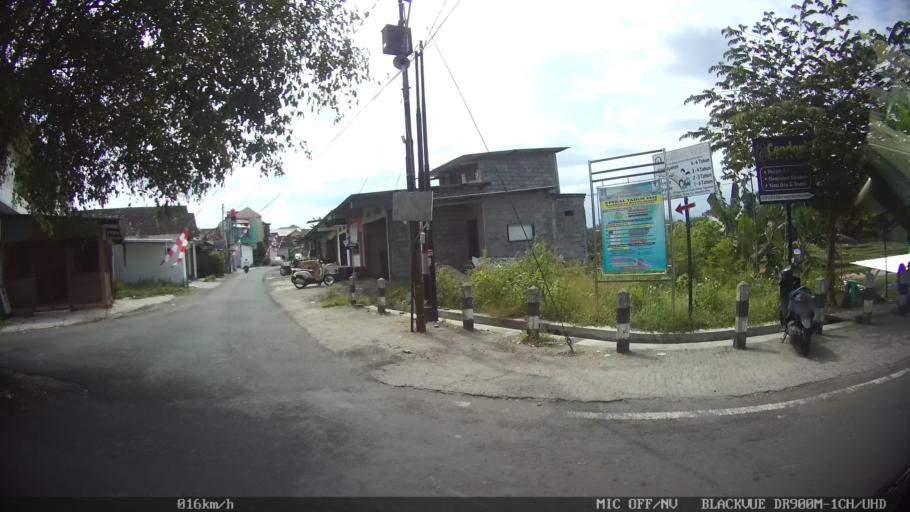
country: ID
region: Daerah Istimewa Yogyakarta
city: Depok
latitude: -7.7733
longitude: 110.4360
